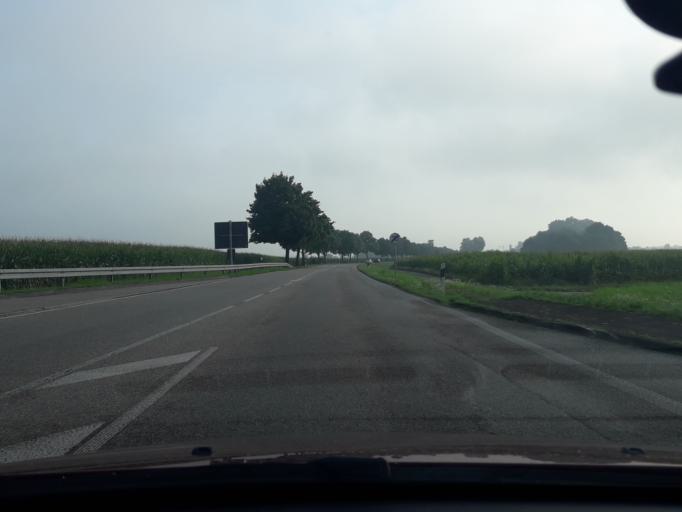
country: DE
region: Baden-Wuerttemberg
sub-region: Karlsruhe Region
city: Lichtenau
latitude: 48.6994
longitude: 7.9809
